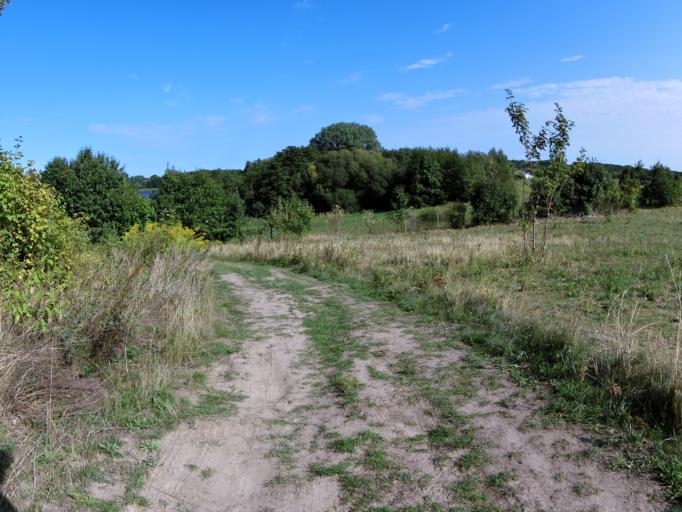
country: DE
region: Mecklenburg-Vorpommern
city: Seebad Bansin
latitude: 53.9638
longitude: 14.1404
